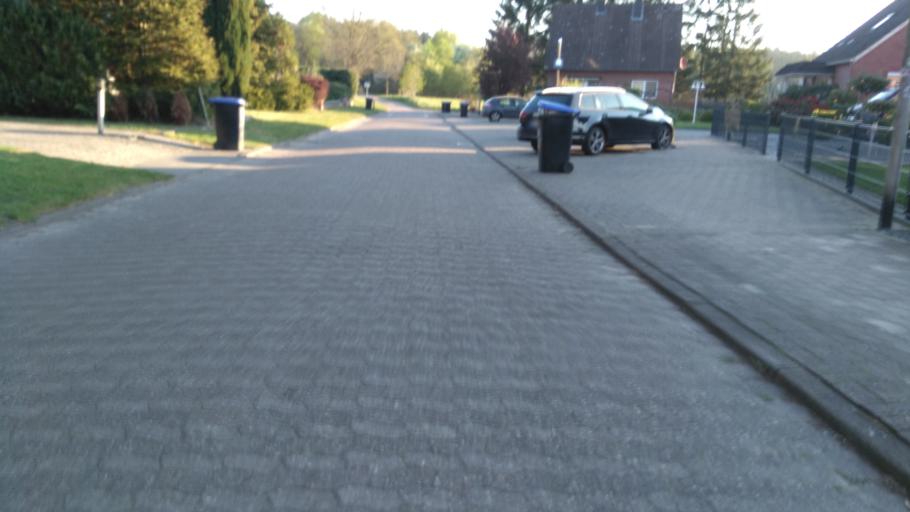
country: DE
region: Lower Saxony
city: Harsefeld
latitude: 53.4699
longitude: 9.5098
